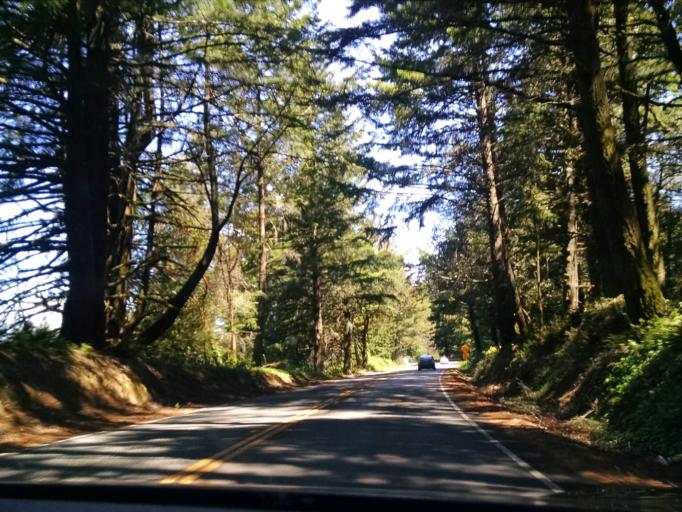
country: US
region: California
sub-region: San Mateo County
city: Highlands-Baywood Park
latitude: 37.4560
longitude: -122.3400
